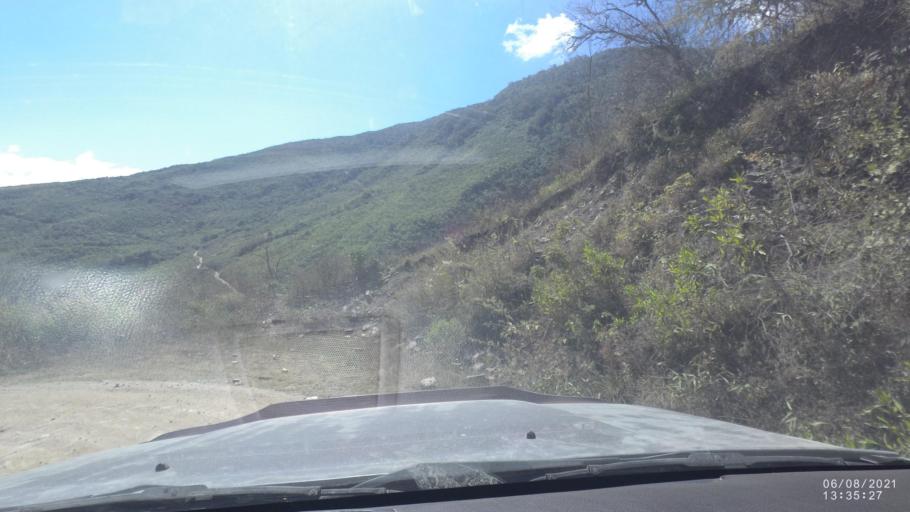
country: BO
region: La Paz
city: Quime
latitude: -16.6916
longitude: -66.7226
